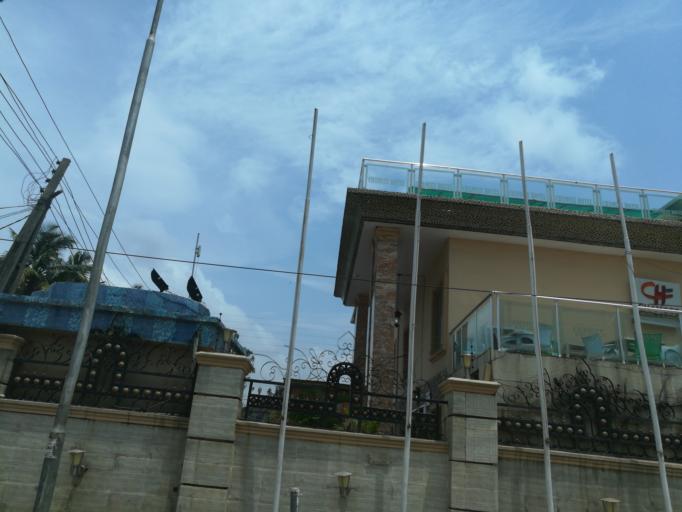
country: NG
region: Lagos
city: Oshodi
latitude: 6.5472
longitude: 3.3314
